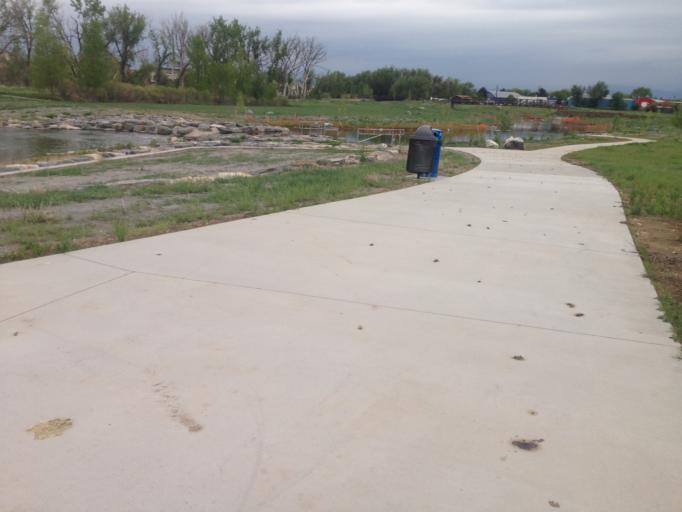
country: US
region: Colorado
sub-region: Boulder County
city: Longmont
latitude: 40.1561
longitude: -105.0974
